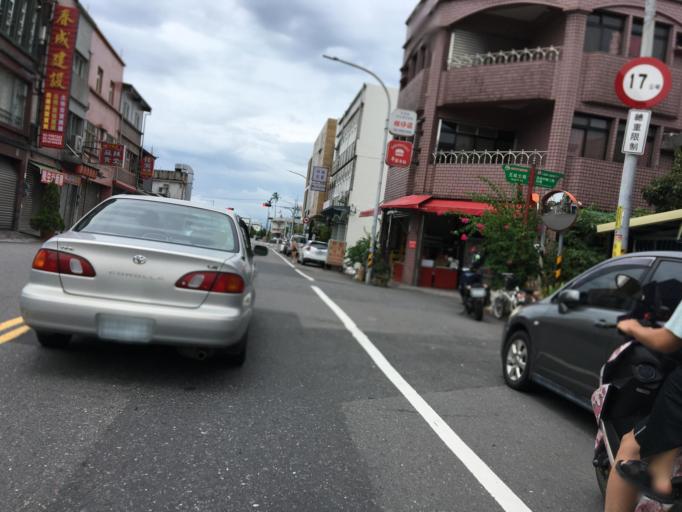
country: TW
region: Taiwan
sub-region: Yilan
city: Yilan
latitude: 24.6858
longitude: 121.7979
